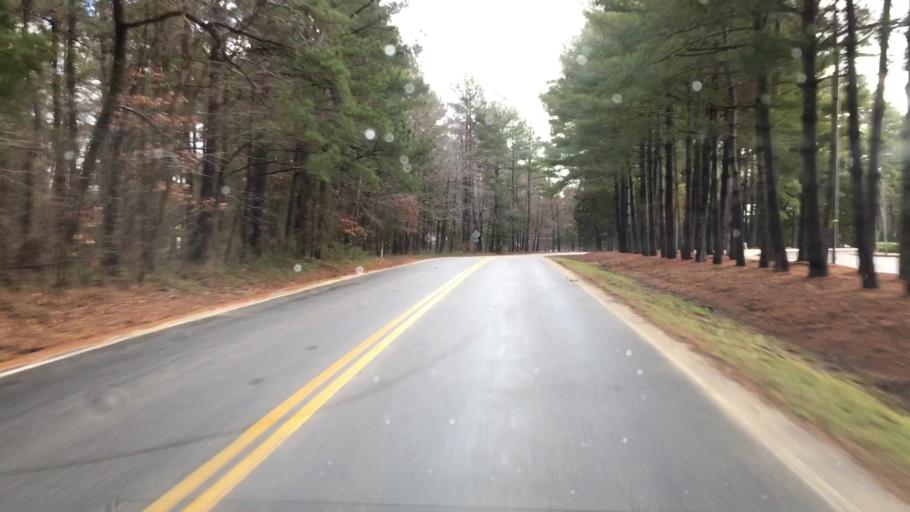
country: US
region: Virginia
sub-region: Chesterfield County
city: Bon Air
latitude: 37.5125
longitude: -77.5965
